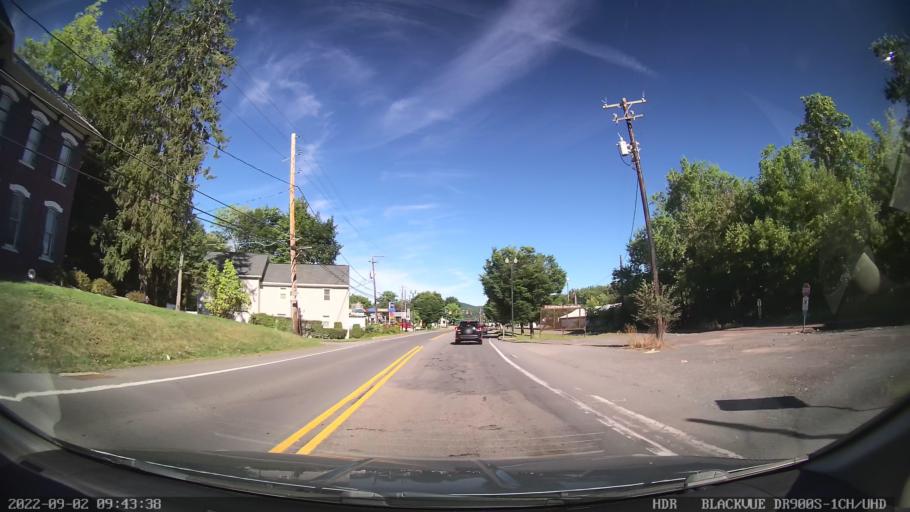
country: US
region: Pennsylvania
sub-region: Northumberland County
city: Riverside
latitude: 40.9545
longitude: -76.6218
